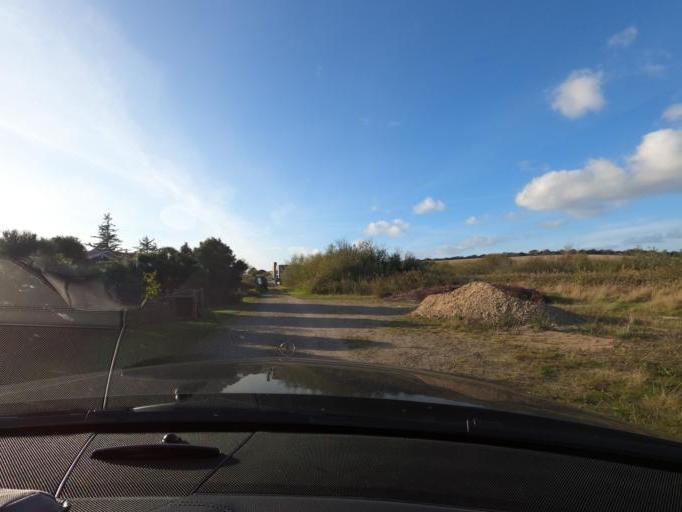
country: DK
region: South Denmark
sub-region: Sonderborg Kommune
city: Horuphav
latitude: 54.8687
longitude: 9.8862
